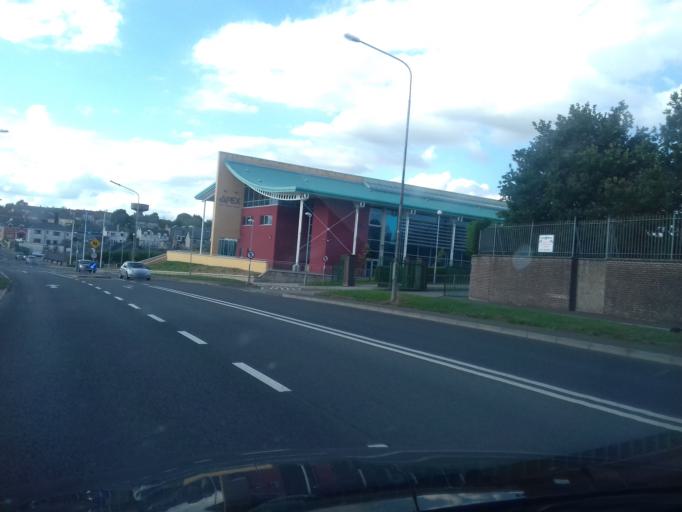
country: IE
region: Leinster
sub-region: Loch Garman
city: New Ross
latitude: 52.3962
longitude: -6.9347
